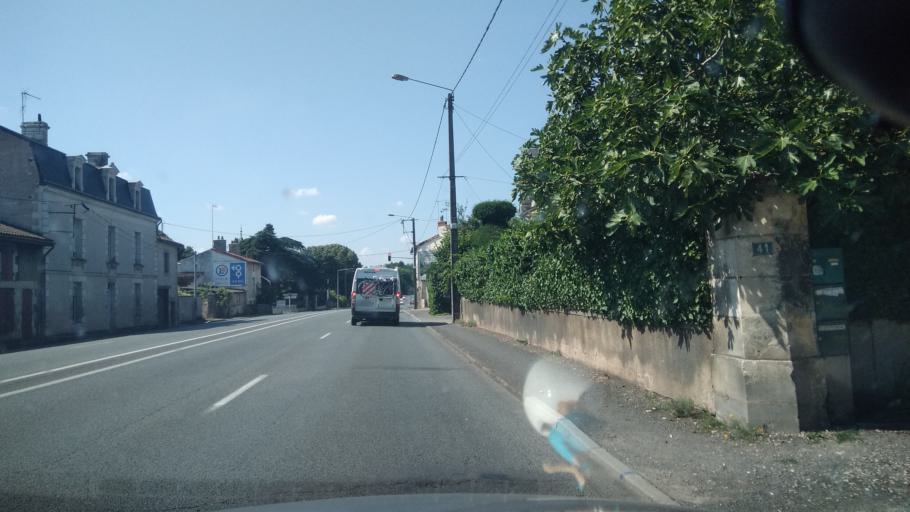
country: FR
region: Poitou-Charentes
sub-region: Departement de la Vienne
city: Chasseneuil-du-Poitou
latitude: 46.6400
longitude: 0.3592
